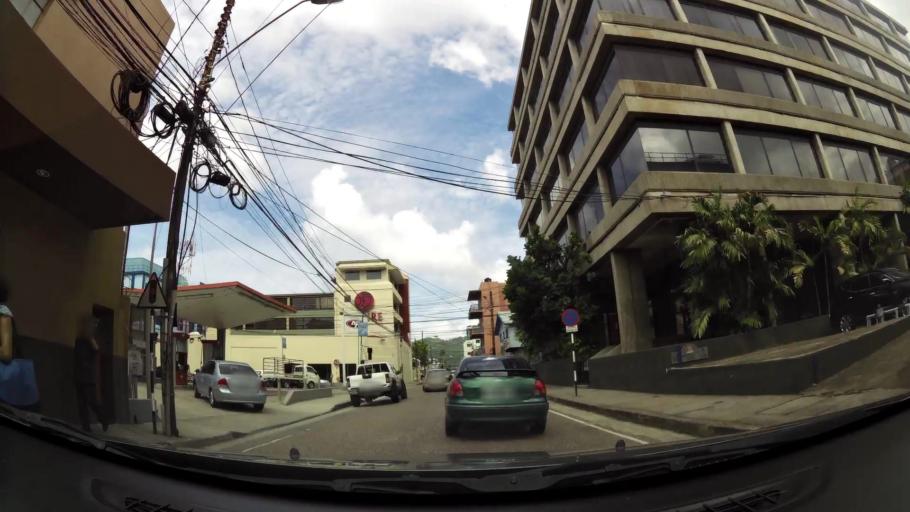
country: TT
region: City of Port of Spain
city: Port-of-Spain
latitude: 10.6562
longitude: -61.5130
